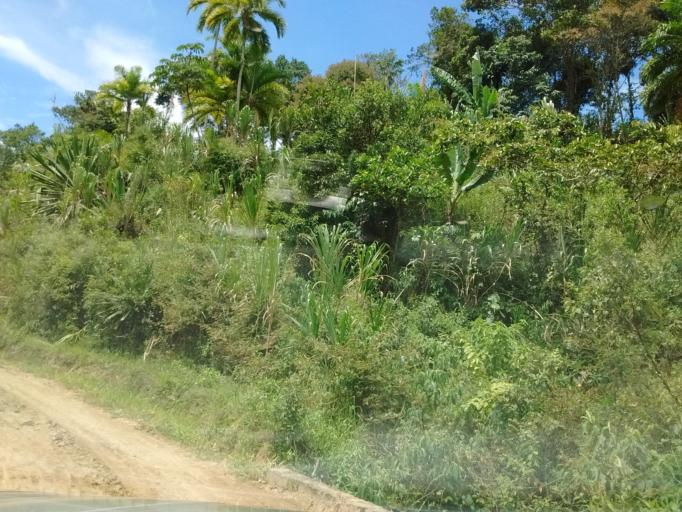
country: CO
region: Cauca
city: Morales
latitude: 2.6727
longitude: -76.7644
